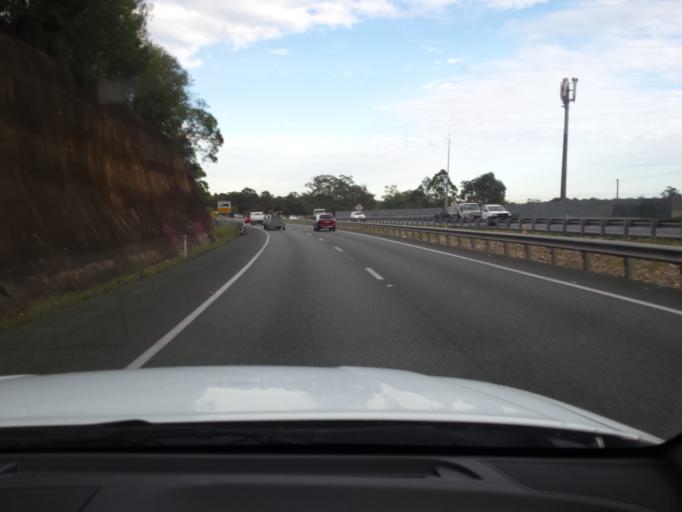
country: AU
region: Queensland
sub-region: Logan
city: Slacks Creek
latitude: -27.6678
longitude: 153.1632
